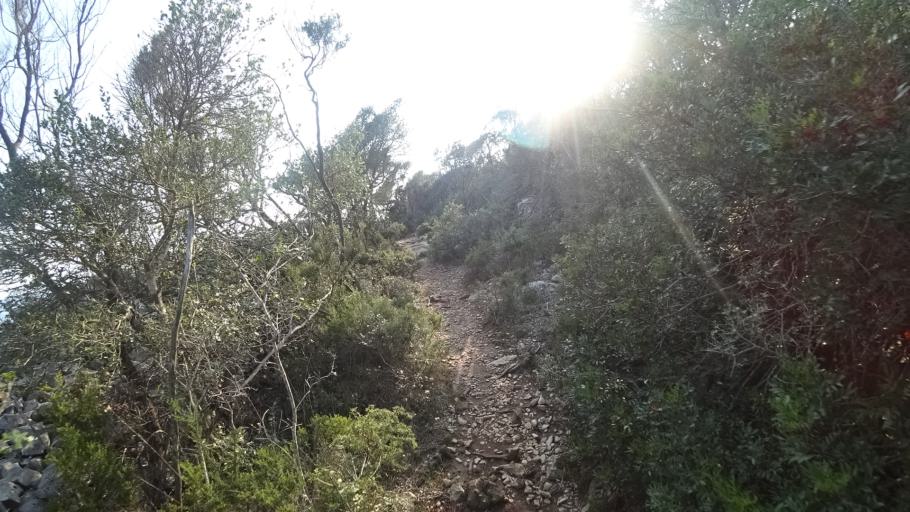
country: HR
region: Primorsko-Goranska
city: Mali Losinj
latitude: 44.5123
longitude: 14.4794
